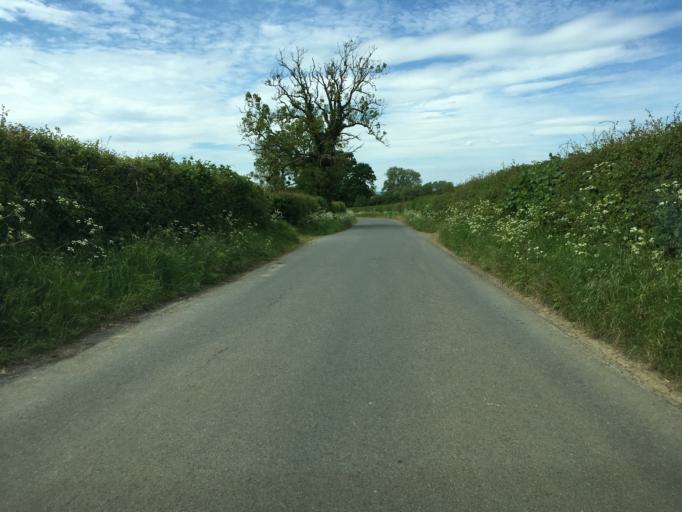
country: GB
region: England
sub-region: South Gloucestershire
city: Charfield
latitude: 51.6651
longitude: -2.3950
